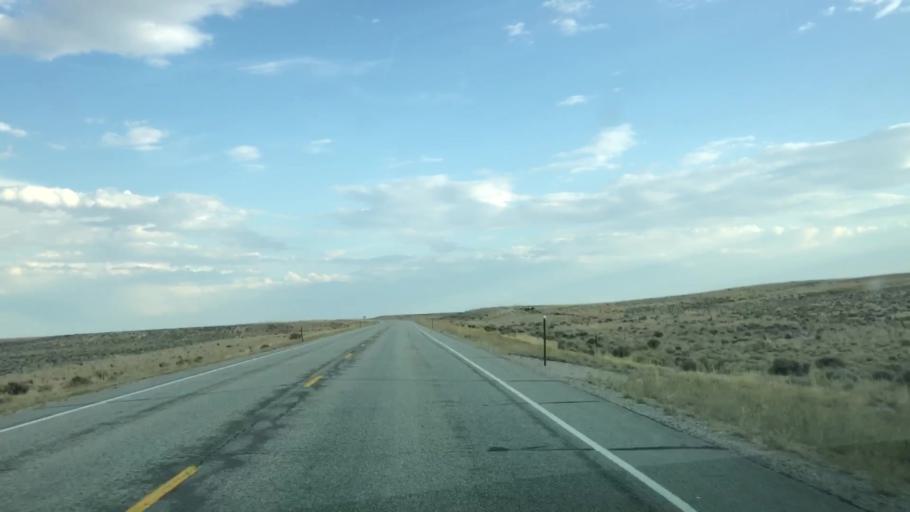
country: US
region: Wyoming
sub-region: Sweetwater County
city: North Rock Springs
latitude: 42.2839
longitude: -109.4873
